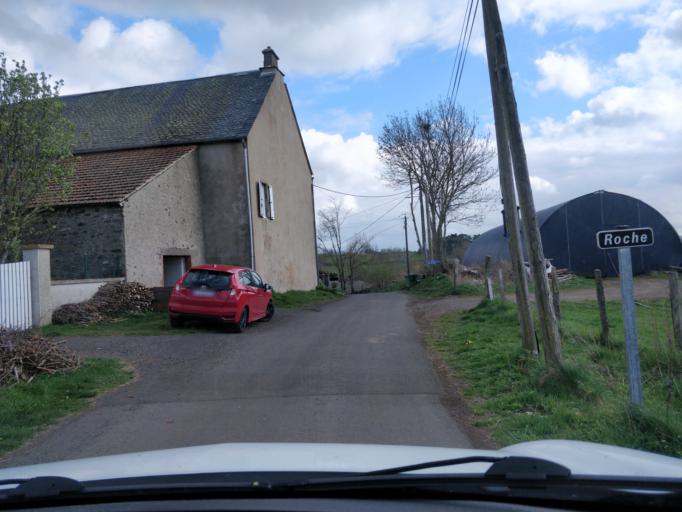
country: FR
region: Auvergne
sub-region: Departement du Cantal
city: Allanche
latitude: 45.2070
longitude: 2.9528
